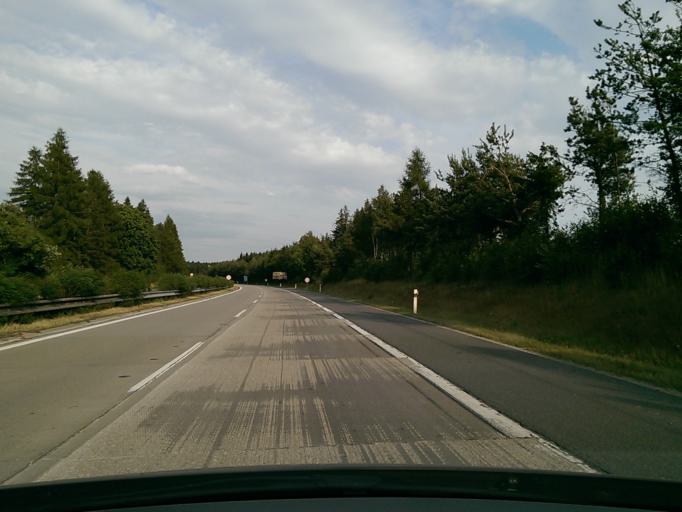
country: CZ
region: Vysocina
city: Luka nad Jihlavou
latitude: 49.4148
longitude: 15.7106
